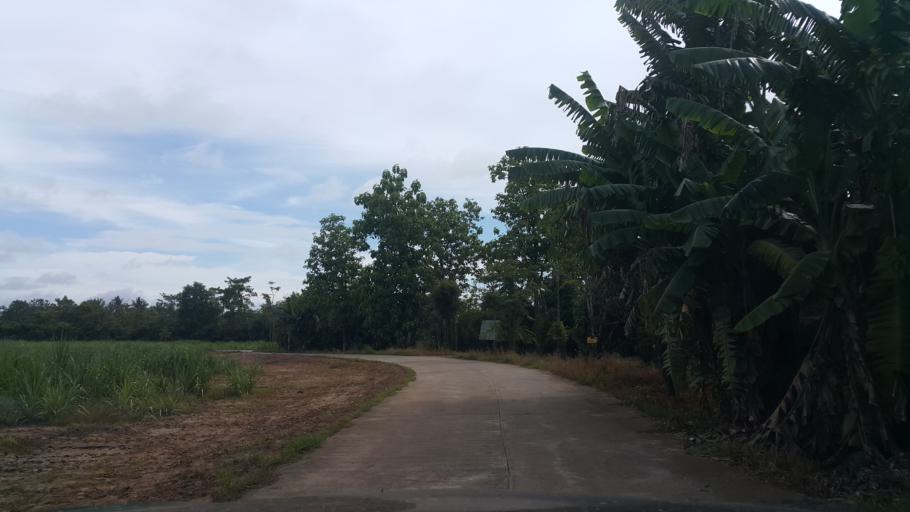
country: TH
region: Sukhothai
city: Sawankhalok
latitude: 17.2744
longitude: 99.9003
